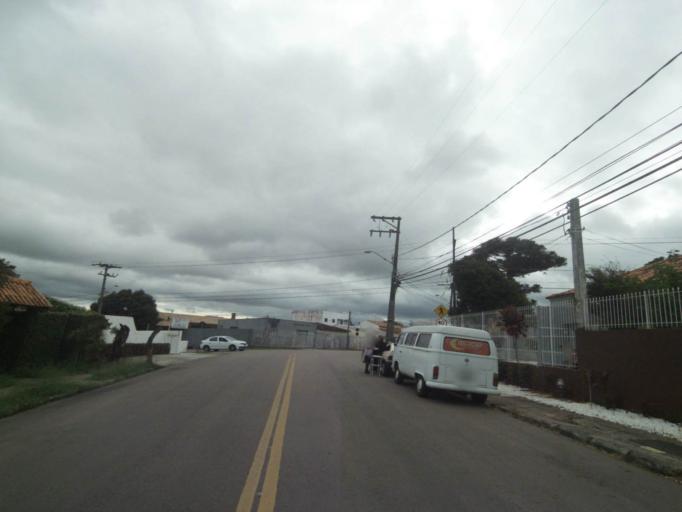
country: BR
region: Parana
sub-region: Curitiba
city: Curitiba
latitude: -25.4851
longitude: -49.2848
